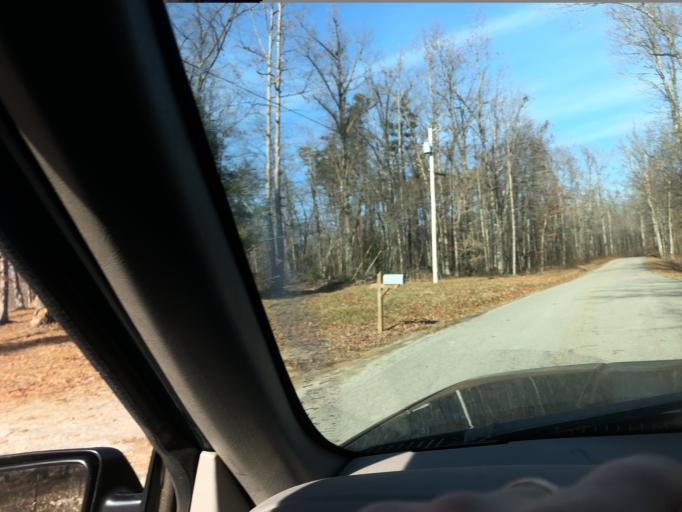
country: US
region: Tennessee
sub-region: Putnam County
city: Monterey
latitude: 35.9903
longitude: -85.2811
